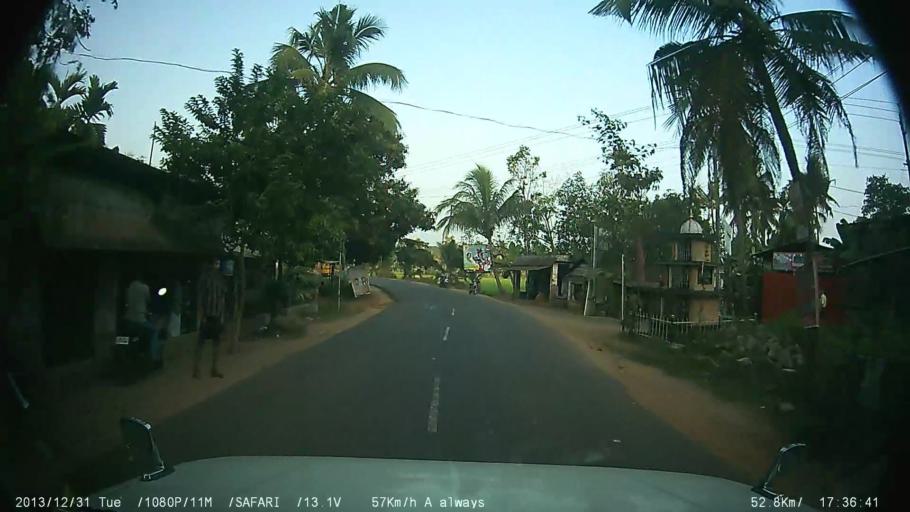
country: IN
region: Kerala
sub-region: Kottayam
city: Vaikam
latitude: 9.6923
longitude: 76.4740
